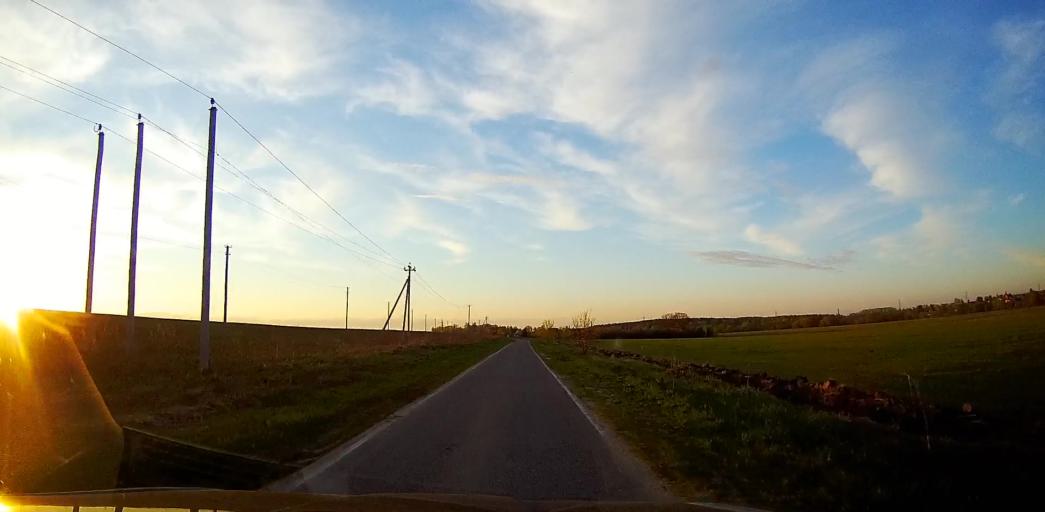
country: RU
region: Moskovskaya
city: Peski
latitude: 55.2229
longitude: 38.7364
